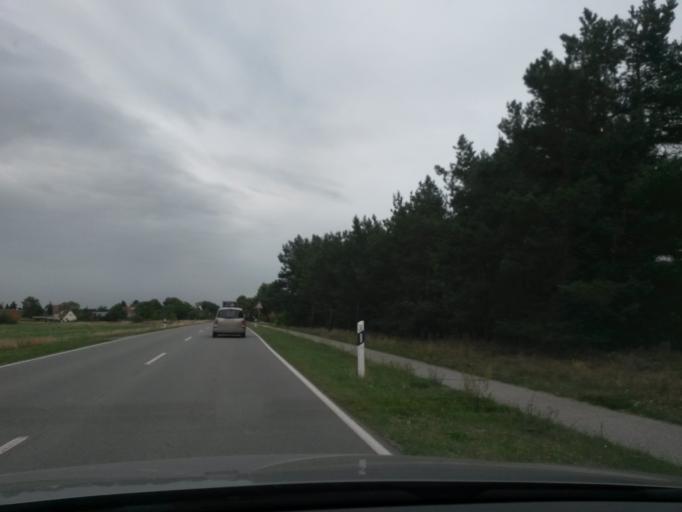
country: DE
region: Saxony-Anhalt
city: Klietz
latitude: 52.6907
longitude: 12.0676
